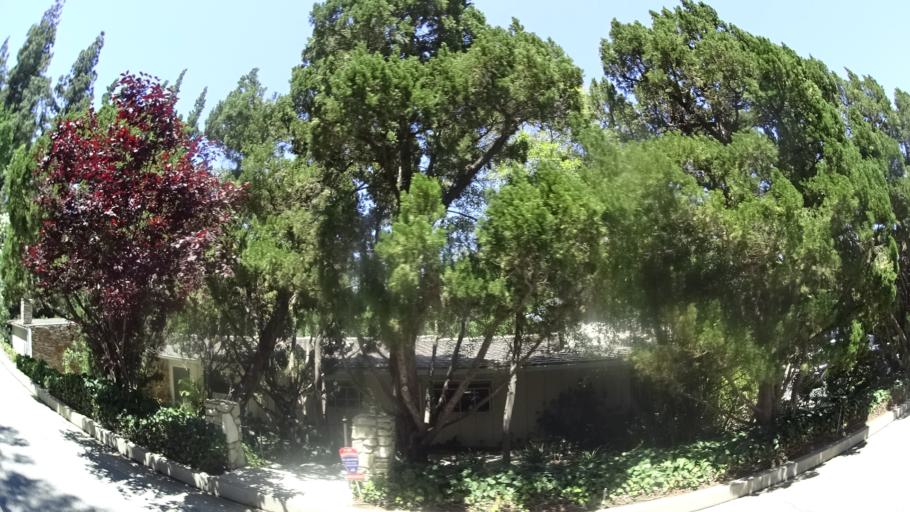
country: US
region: California
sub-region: Los Angeles County
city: Sherman Oaks
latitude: 34.1443
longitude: -118.4830
